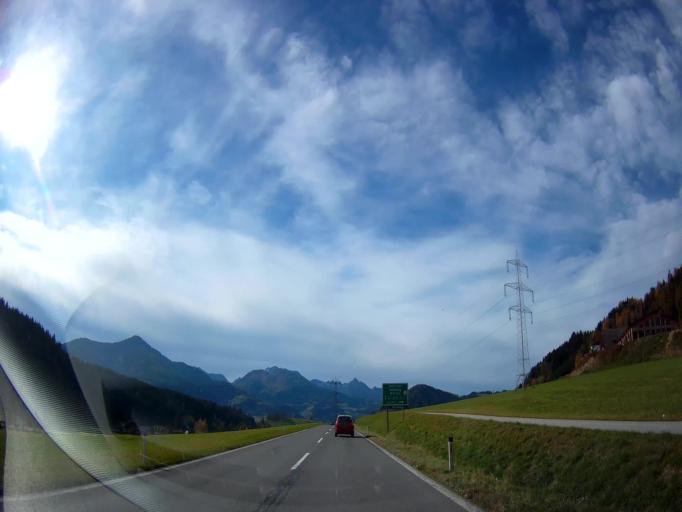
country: AT
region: Styria
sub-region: Politischer Bezirk Liezen
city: Grobming
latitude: 47.4596
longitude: 13.9219
